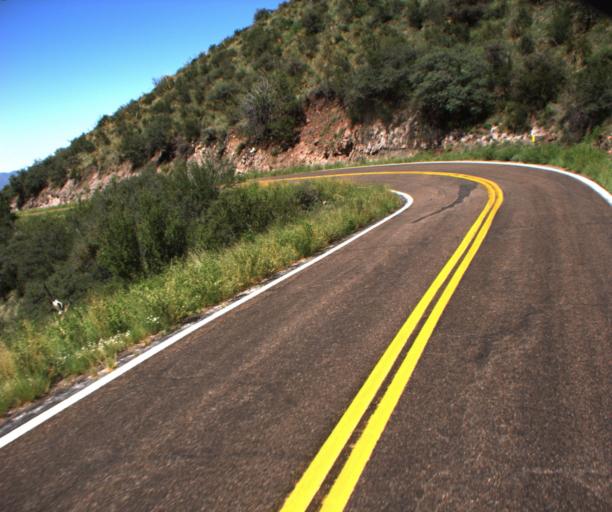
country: US
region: Arizona
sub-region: Greenlee County
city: Morenci
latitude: 33.2253
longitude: -109.3896
